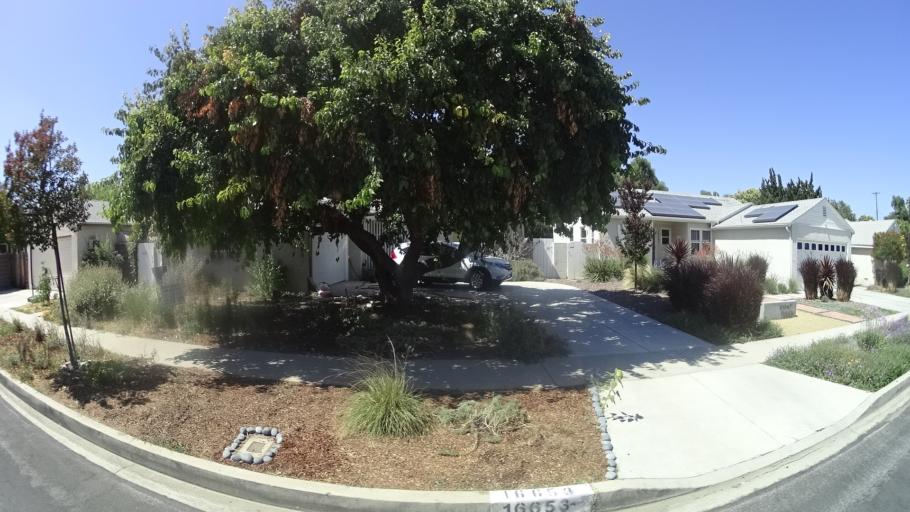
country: US
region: California
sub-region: Los Angeles County
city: Van Nuys
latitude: 34.1884
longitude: -118.4963
